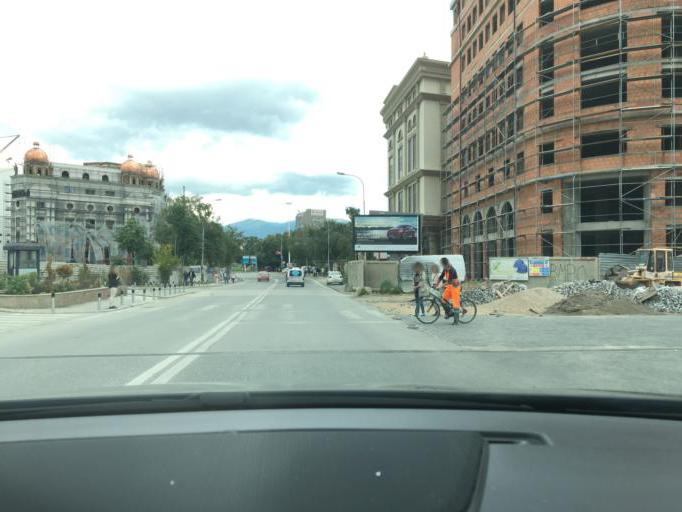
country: MK
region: Karpos
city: Skopje
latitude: 41.9955
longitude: 21.4374
